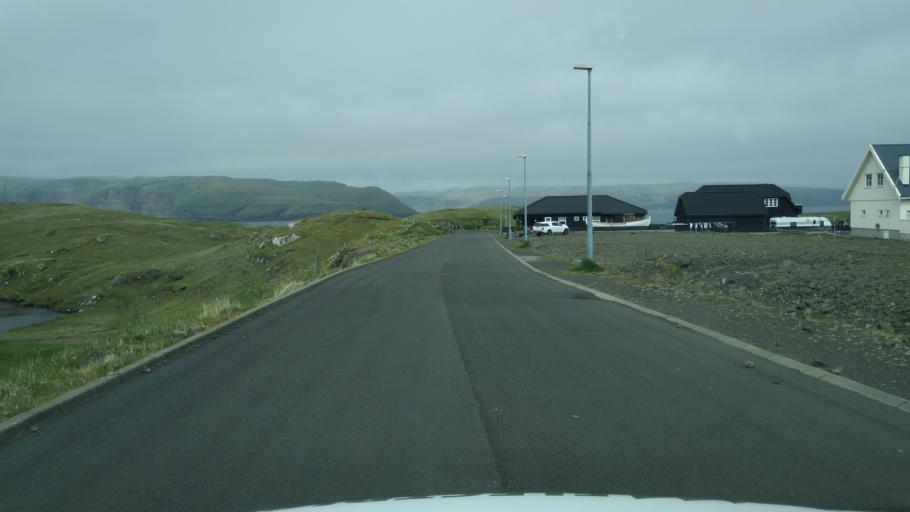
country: FO
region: Sandoy
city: Sandur
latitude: 61.9044
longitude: -6.8932
